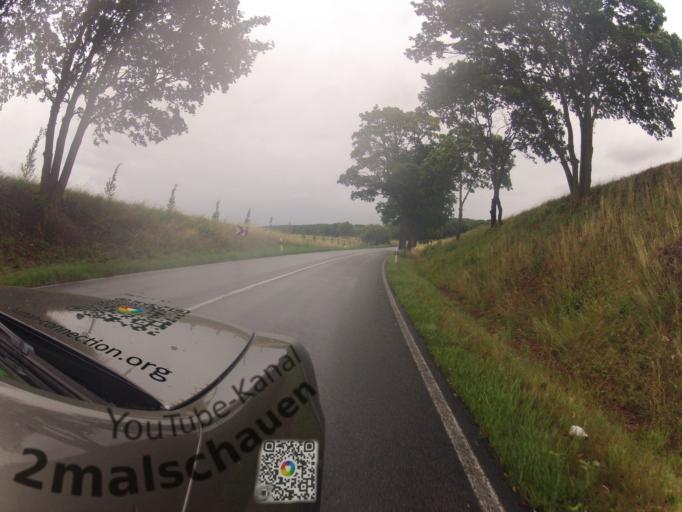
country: DE
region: Mecklenburg-Vorpommern
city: Seebad Heringsdorf
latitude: 53.8987
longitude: 14.1451
